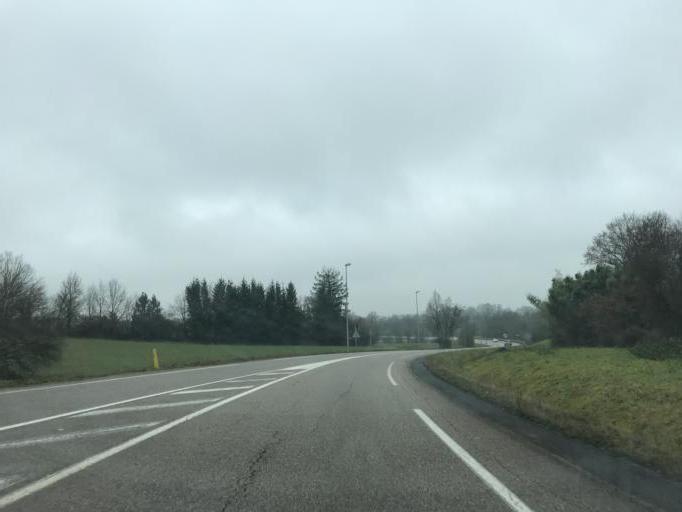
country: FR
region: Rhone-Alpes
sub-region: Departement de l'Ain
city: Peronnas
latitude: 46.1904
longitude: 5.1965
